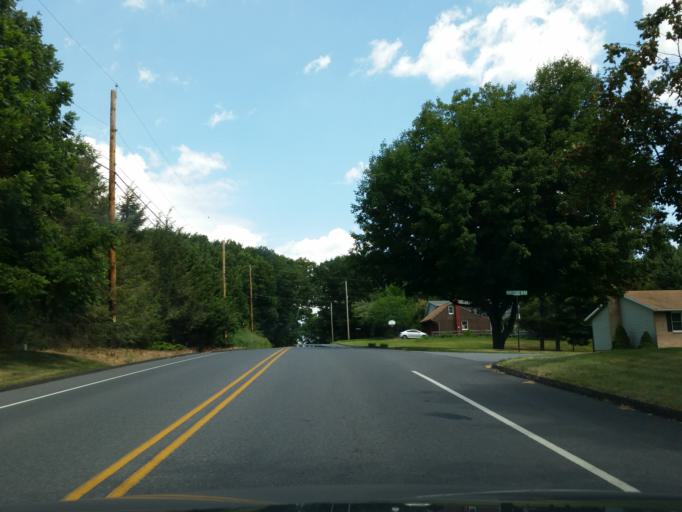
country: US
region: Pennsylvania
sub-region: Lebanon County
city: Annville
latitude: 40.3396
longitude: -76.5178
